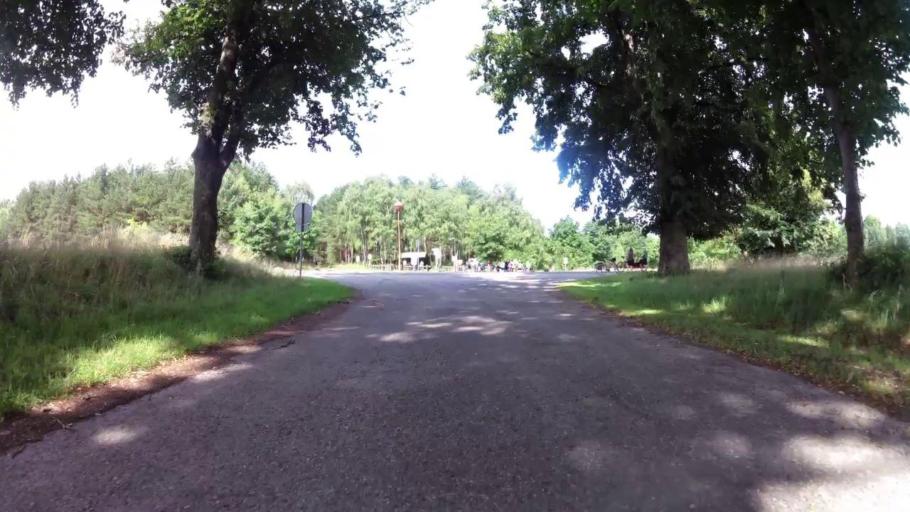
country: PL
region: West Pomeranian Voivodeship
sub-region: Powiat stargardzki
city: Insko
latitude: 53.3791
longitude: 15.5993
